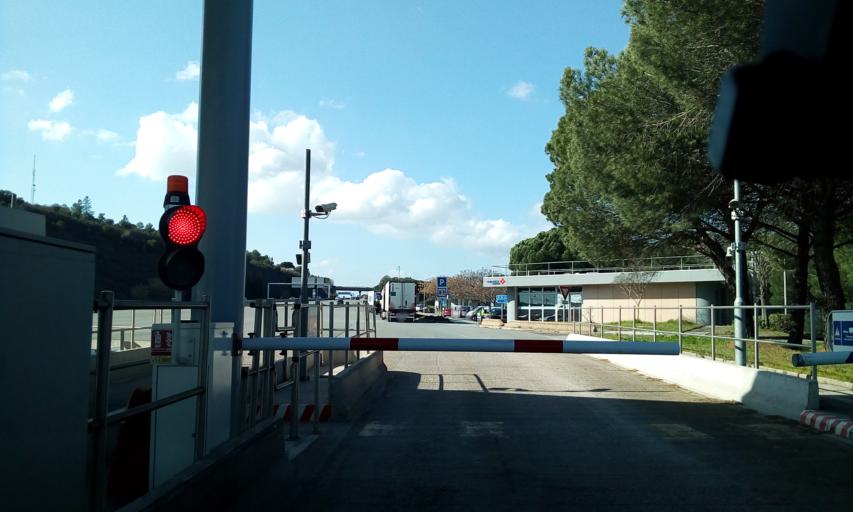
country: FR
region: Provence-Alpes-Cote d'Azur
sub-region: Departement du Var
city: Frejus
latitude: 43.4694
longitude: 6.7291
